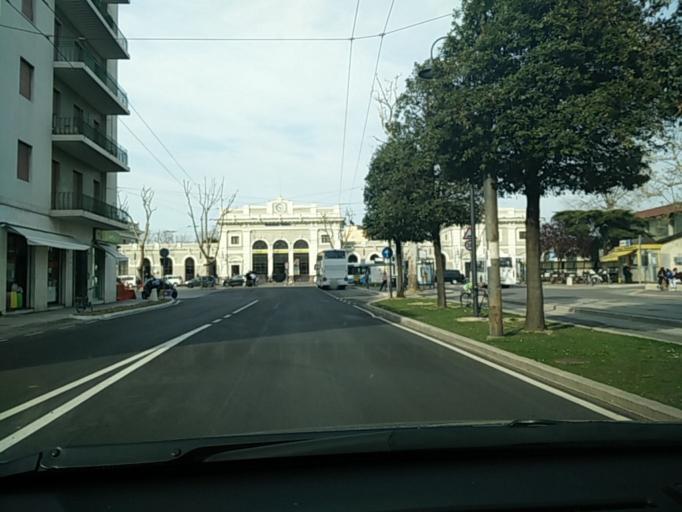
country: IT
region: Emilia-Romagna
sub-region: Provincia di Rimini
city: Rimini
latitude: 44.0632
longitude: 12.5732
